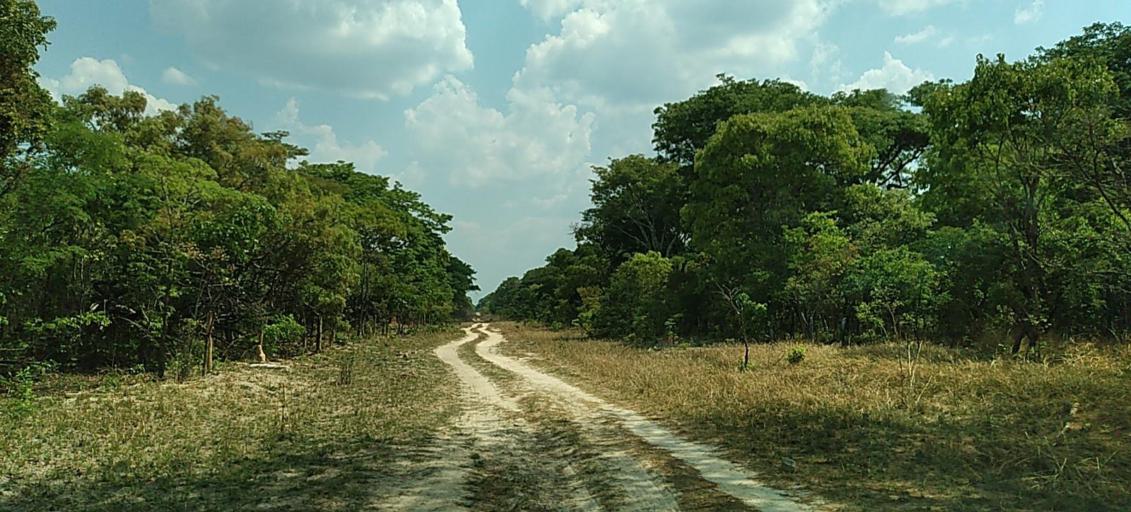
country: ZM
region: Copperbelt
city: Mpongwe
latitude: -13.8358
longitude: 27.9378
